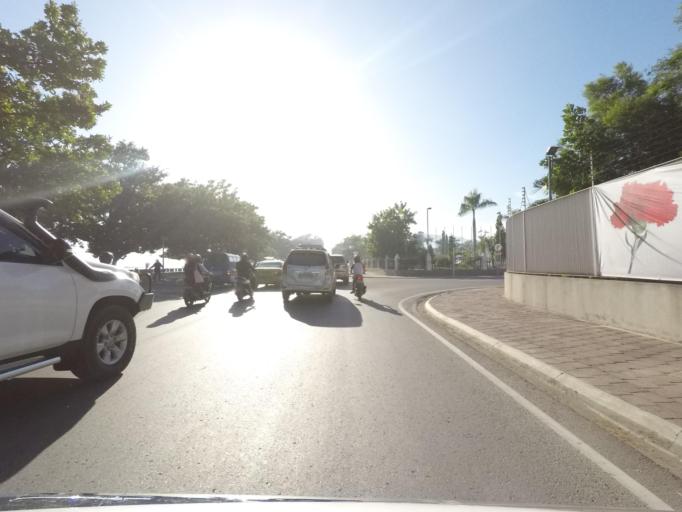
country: TL
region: Dili
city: Dili
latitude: -8.5537
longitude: 125.5771
